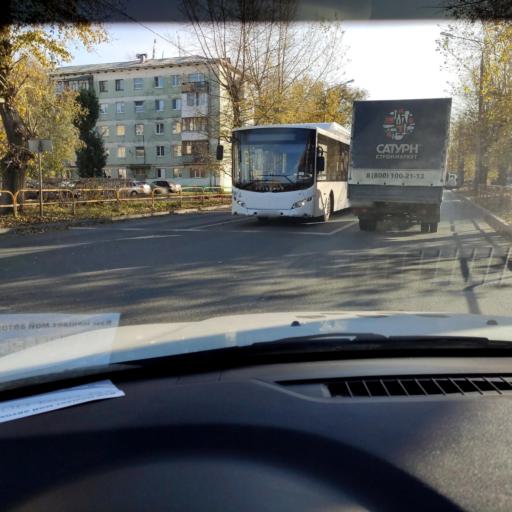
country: RU
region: Samara
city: Tol'yatti
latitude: 53.5375
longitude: 49.4099
